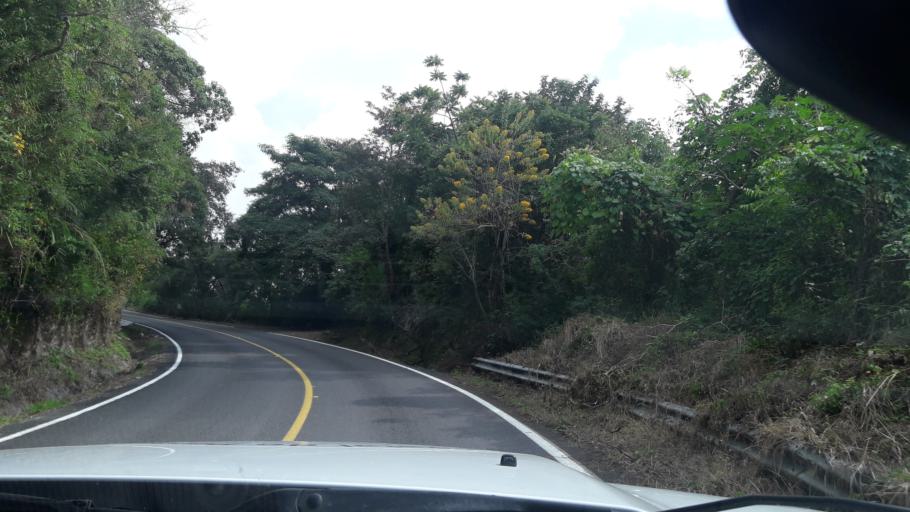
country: MX
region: Colima
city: Suchitlan
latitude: 19.4341
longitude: -103.7142
